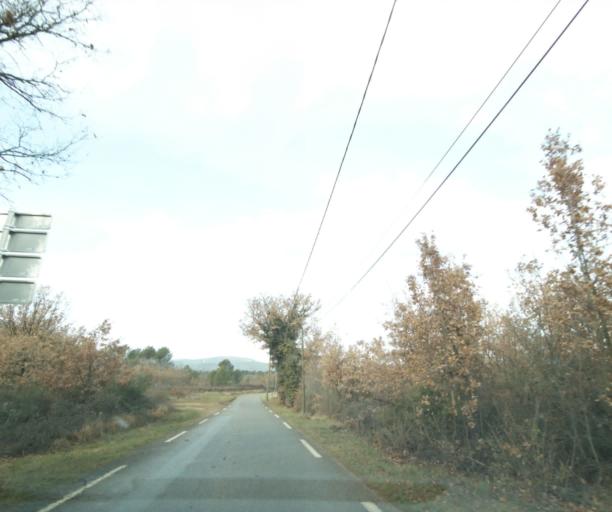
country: FR
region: Provence-Alpes-Cote d'Azur
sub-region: Departement du Var
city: Rougiers
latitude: 43.3993
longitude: 5.8838
